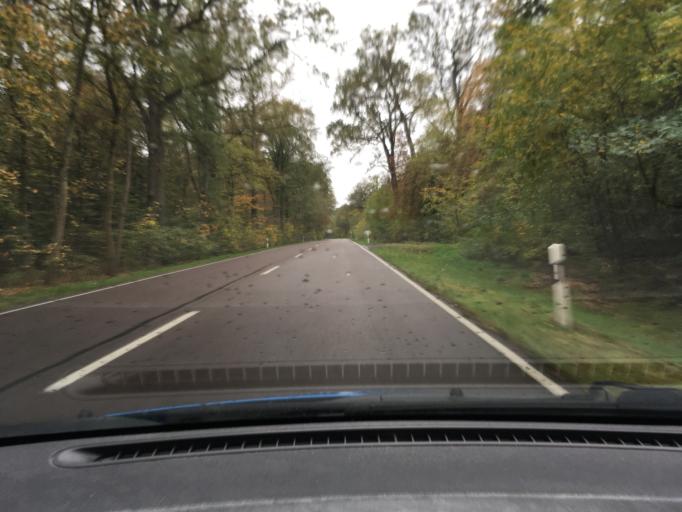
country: DE
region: Saxony-Anhalt
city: Klieken
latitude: 51.8884
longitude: 12.3174
